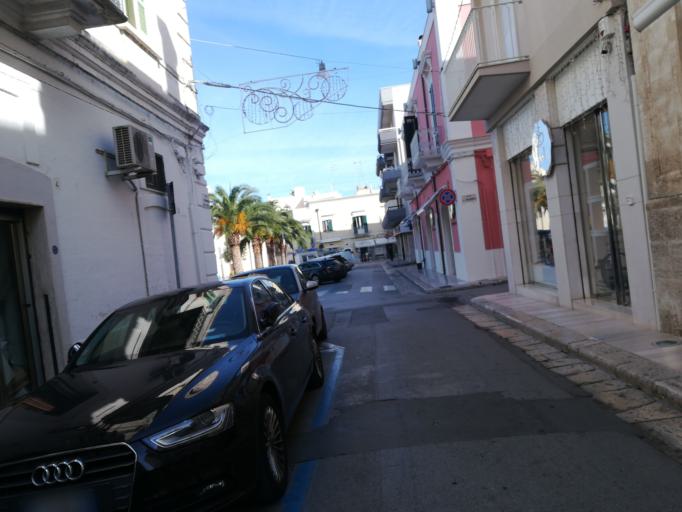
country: IT
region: Apulia
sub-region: Provincia di Bari
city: Polignano a Mare
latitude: 40.9940
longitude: 17.2202
